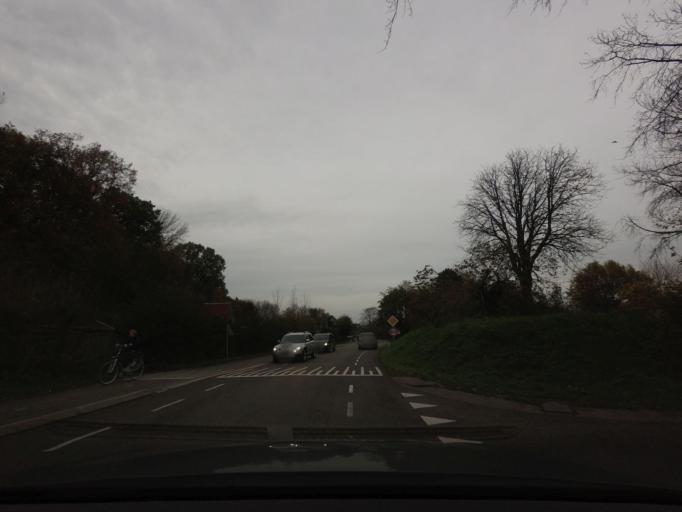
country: NL
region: North Holland
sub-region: Gemeente Bergen
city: Egmond aan Zee
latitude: 52.6400
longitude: 4.6575
